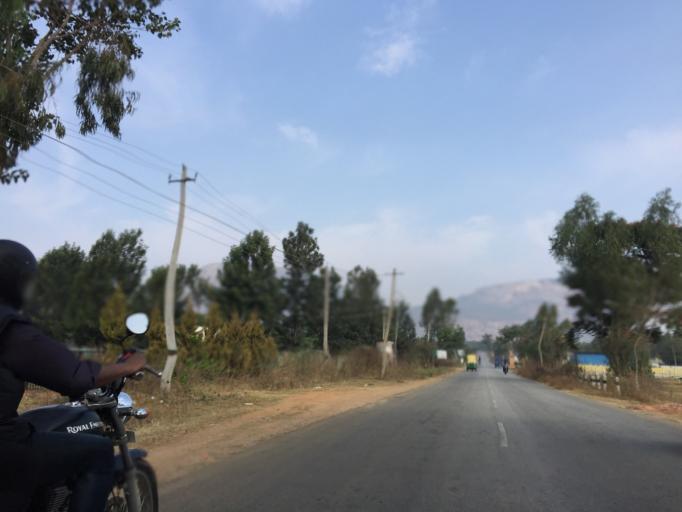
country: IN
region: Karnataka
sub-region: Bangalore Rural
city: Devanhalli
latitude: 13.3331
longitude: 77.6904
